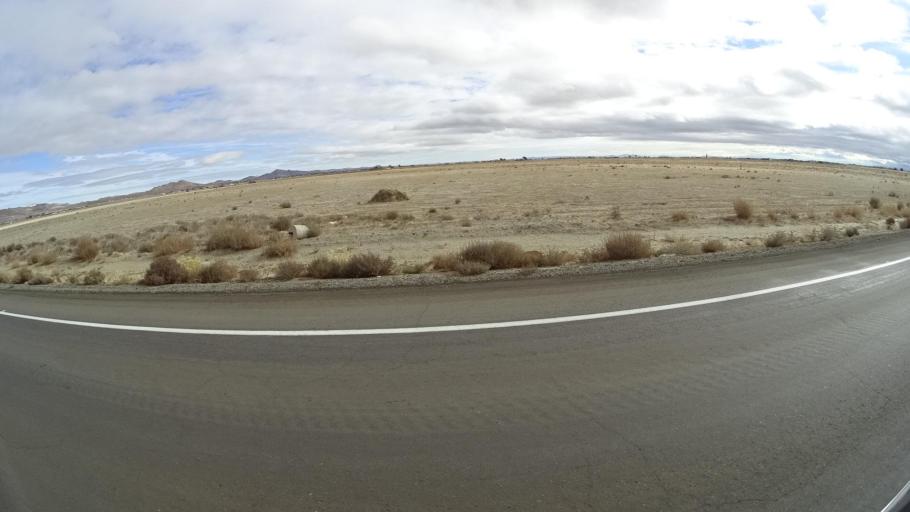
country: US
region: California
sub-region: Kern County
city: Rosamond
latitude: 34.8444
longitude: -118.2908
